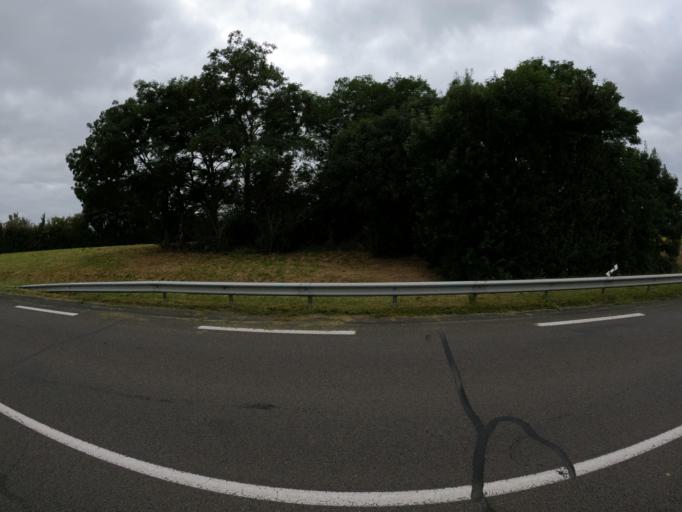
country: FR
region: Pays de la Loire
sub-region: Departement de la Vendee
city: Sainte-Hermine
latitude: 46.5498
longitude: -1.0398
